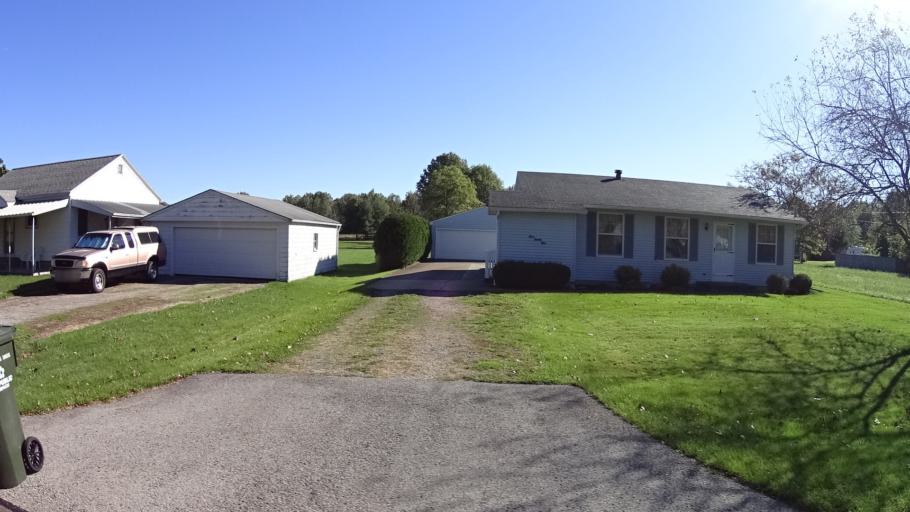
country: US
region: Ohio
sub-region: Lorain County
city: South Amherst
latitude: 41.3435
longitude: -82.2302
